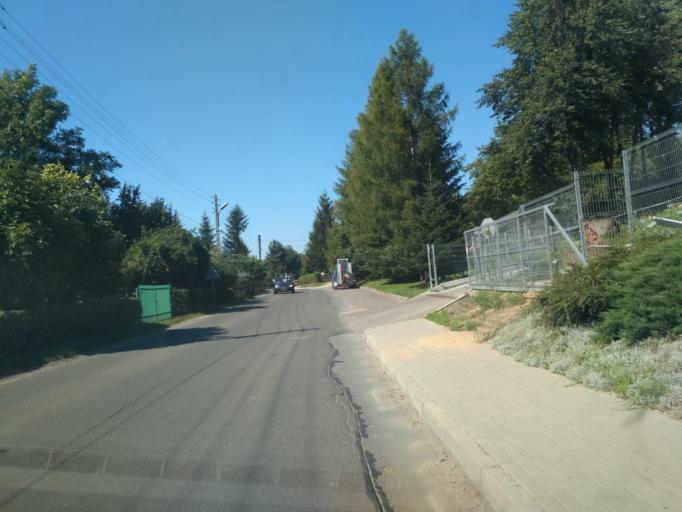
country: PL
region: Subcarpathian Voivodeship
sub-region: Krosno
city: Krosno
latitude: 49.6626
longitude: 21.7524
